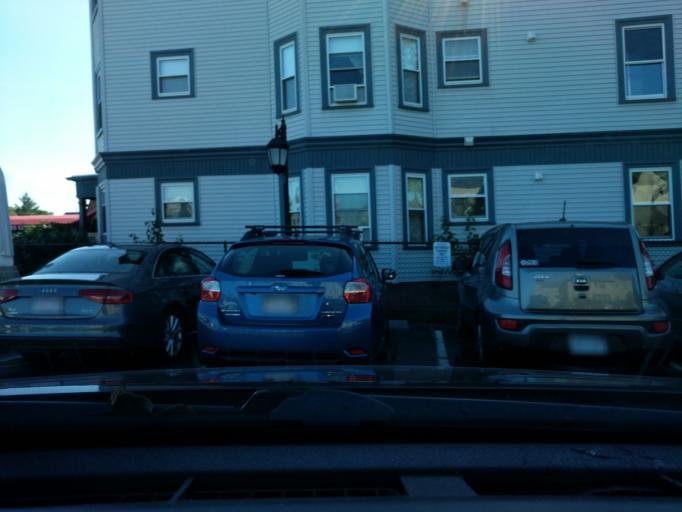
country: US
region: Massachusetts
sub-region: Middlesex County
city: Somerville
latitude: 42.3939
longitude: -71.1268
